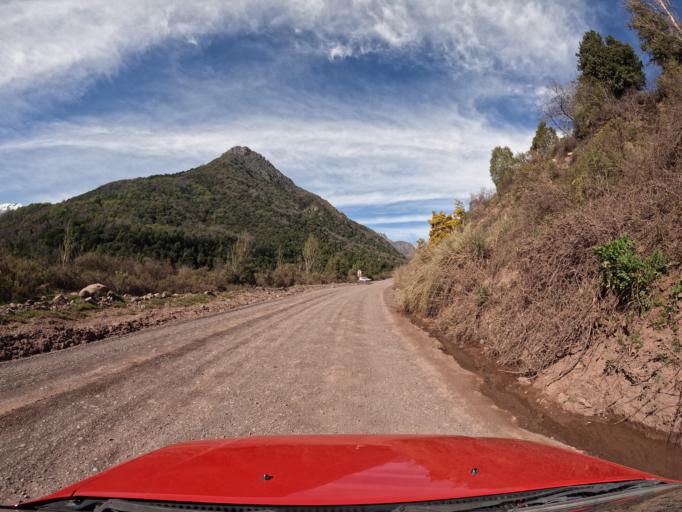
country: CL
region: O'Higgins
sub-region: Provincia de Colchagua
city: Chimbarongo
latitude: -35.0012
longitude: -70.7624
